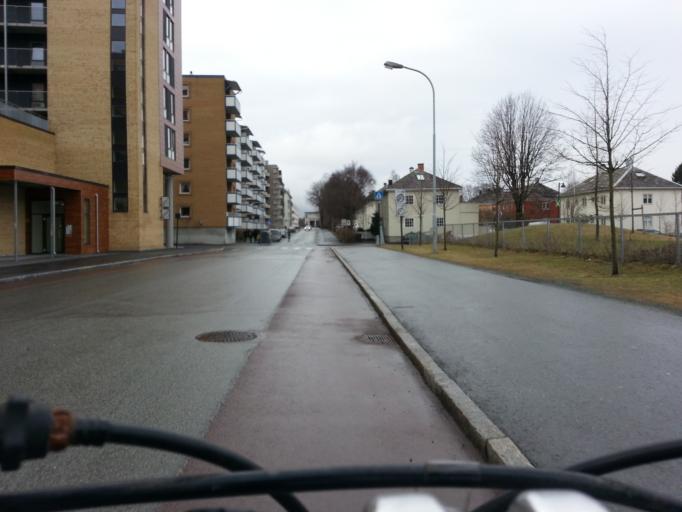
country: NO
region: Sor-Trondelag
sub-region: Trondheim
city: Trondheim
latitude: 63.4194
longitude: 10.3942
